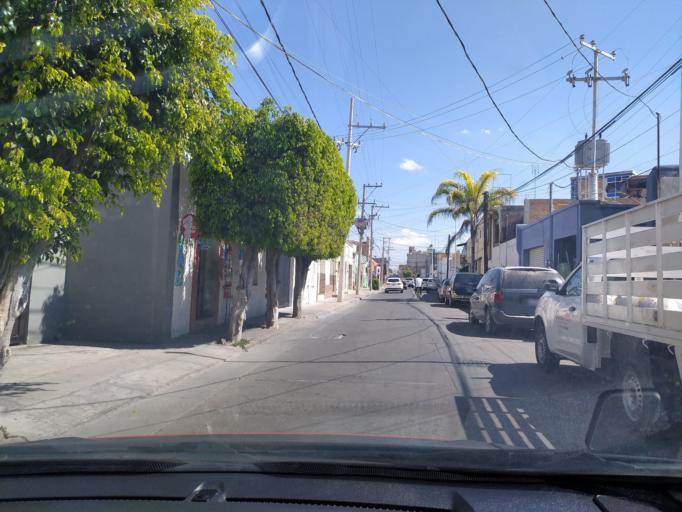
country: LA
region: Oudomxai
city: Muang La
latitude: 21.0169
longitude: 101.8621
